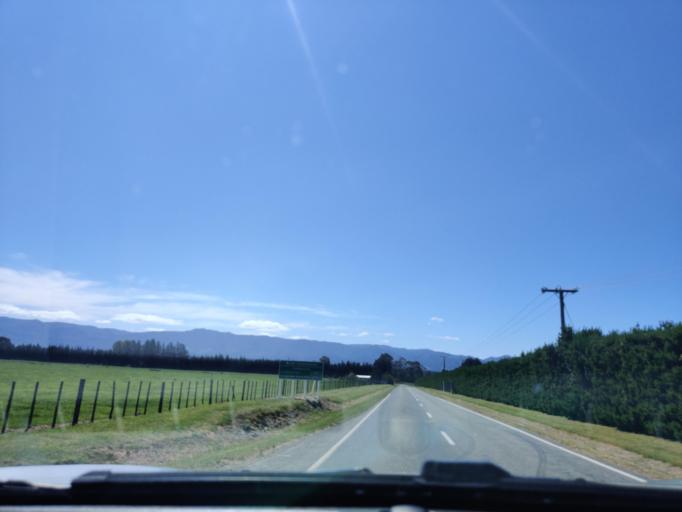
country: NZ
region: Wellington
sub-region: South Wairarapa District
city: Waipawa
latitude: -41.3053
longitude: 175.2733
